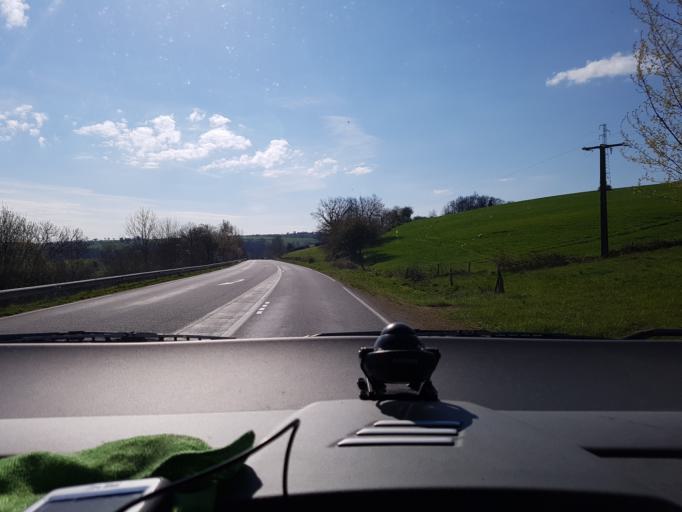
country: FR
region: Midi-Pyrenees
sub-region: Departement de l'Aveyron
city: Moyrazes
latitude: 44.3830
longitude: 2.4064
